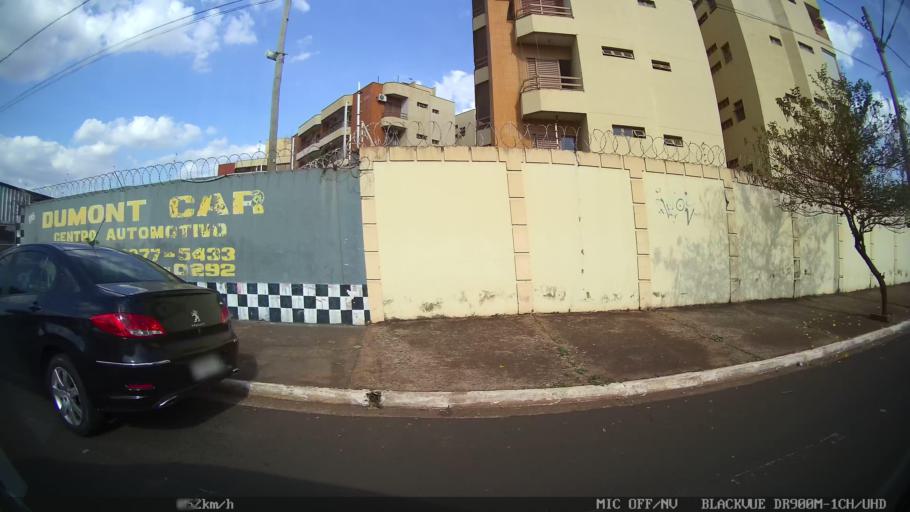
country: BR
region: Sao Paulo
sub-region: Ribeirao Preto
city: Ribeirao Preto
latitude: -21.1791
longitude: -47.8242
